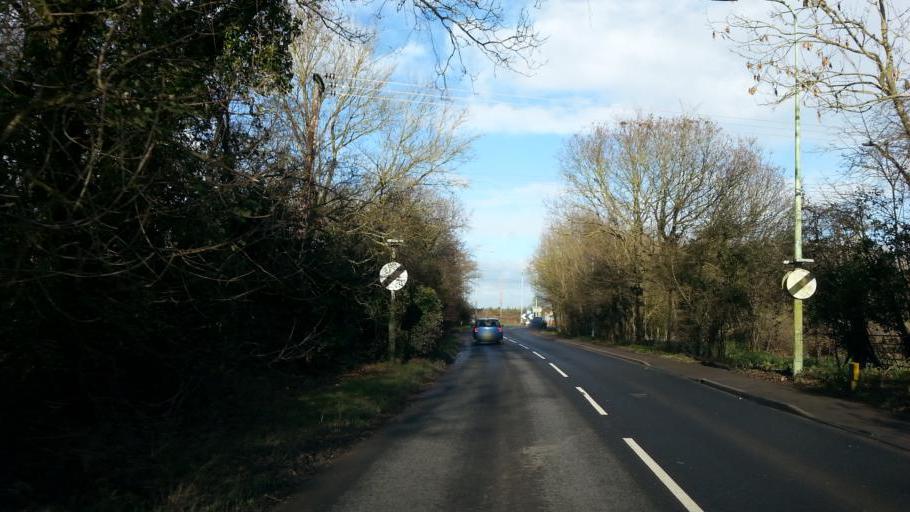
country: GB
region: England
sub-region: Suffolk
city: Halesworth
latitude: 52.3559
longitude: 1.5115
